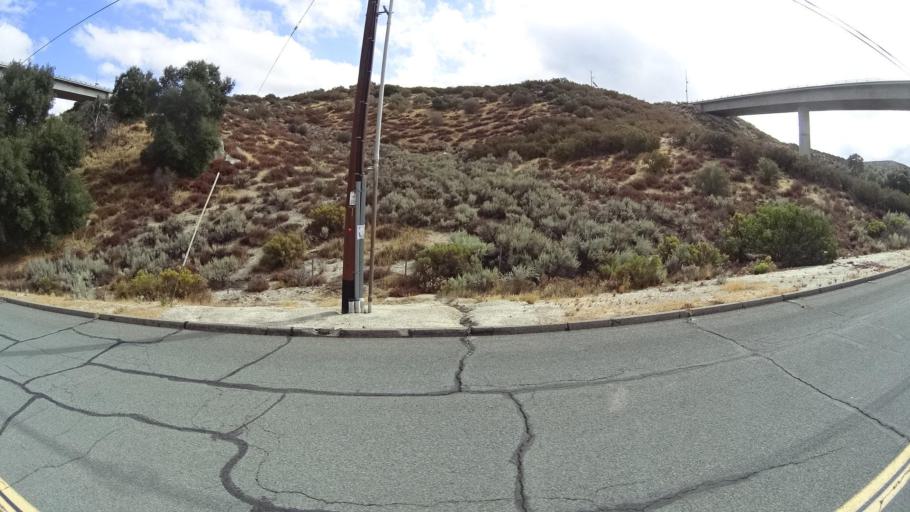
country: US
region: California
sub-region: San Diego County
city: Campo
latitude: 32.7270
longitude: -116.4268
